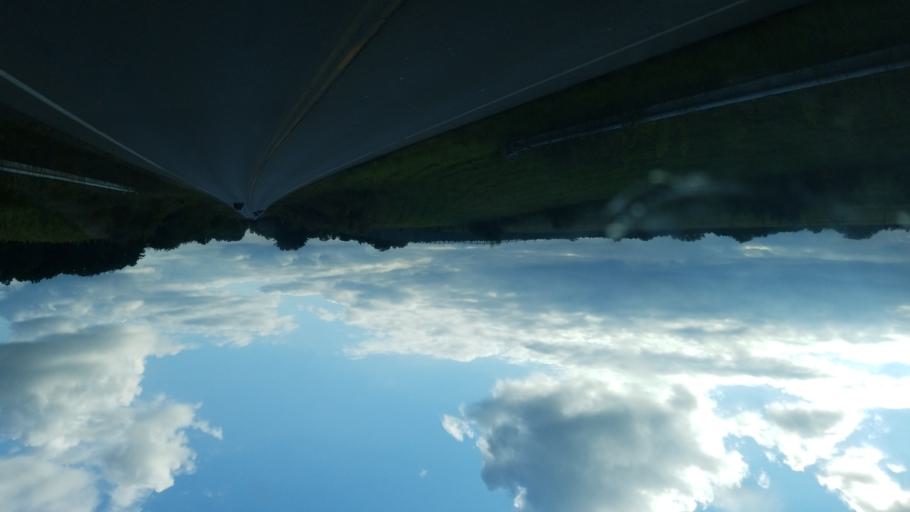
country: US
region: Ohio
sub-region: Richland County
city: Lincoln Heights
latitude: 40.8255
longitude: -82.5027
